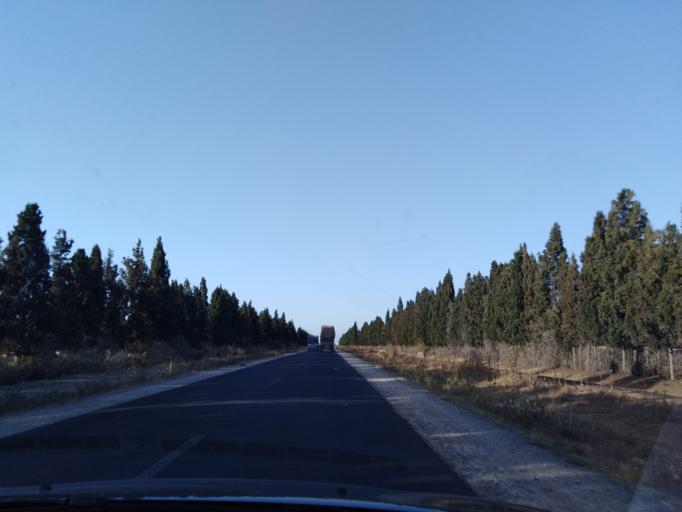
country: MA
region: Doukkala-Abda
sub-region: Safi
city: Safi
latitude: 32.5006
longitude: -8.9251
